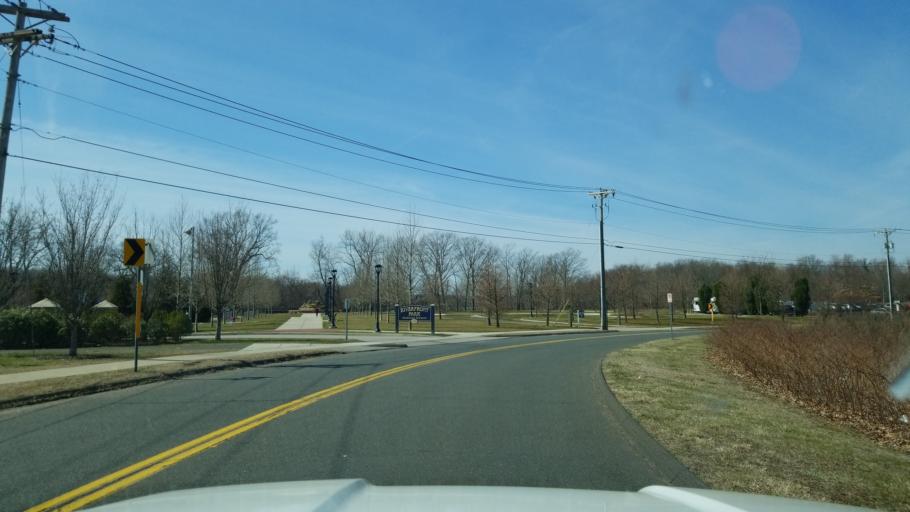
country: US
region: Connecticut
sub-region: Hartford County
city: Glastonbury
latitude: 41.7128
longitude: -72.6155
